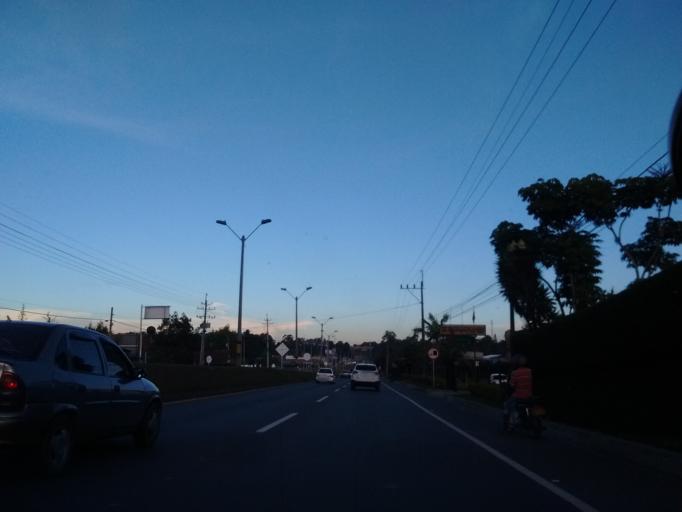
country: CO
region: Antioquia
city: Rionegro
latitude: 6.1866
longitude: -75.3785
